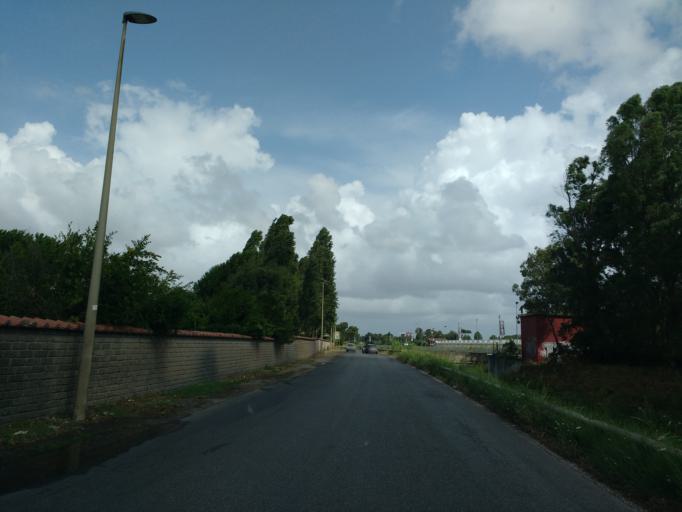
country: IT
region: Latium
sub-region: Citta metropolitana di Roma Capitale
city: Acilia-Castel Fusano-Ostia Antica
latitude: 41.7604
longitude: 12.3294
